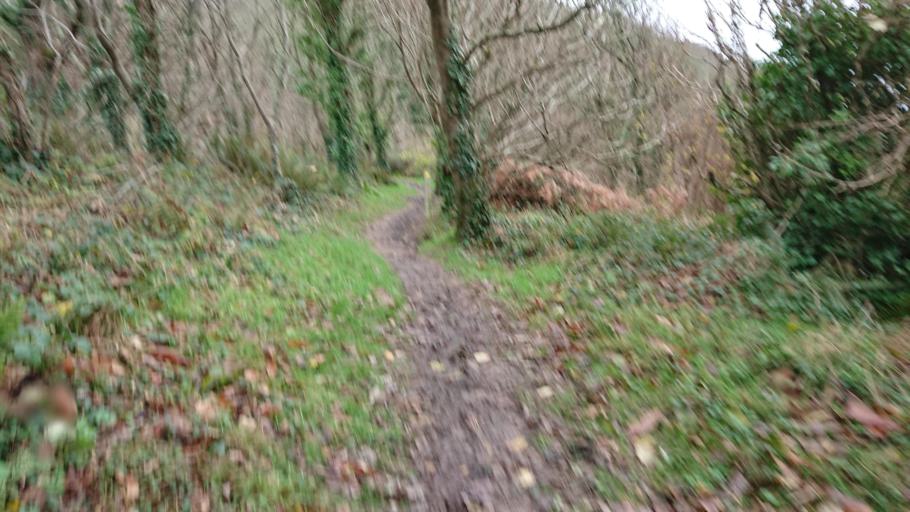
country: GB
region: England
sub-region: Cornwall
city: Fowey
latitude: 50.3355
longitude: -4.5771
